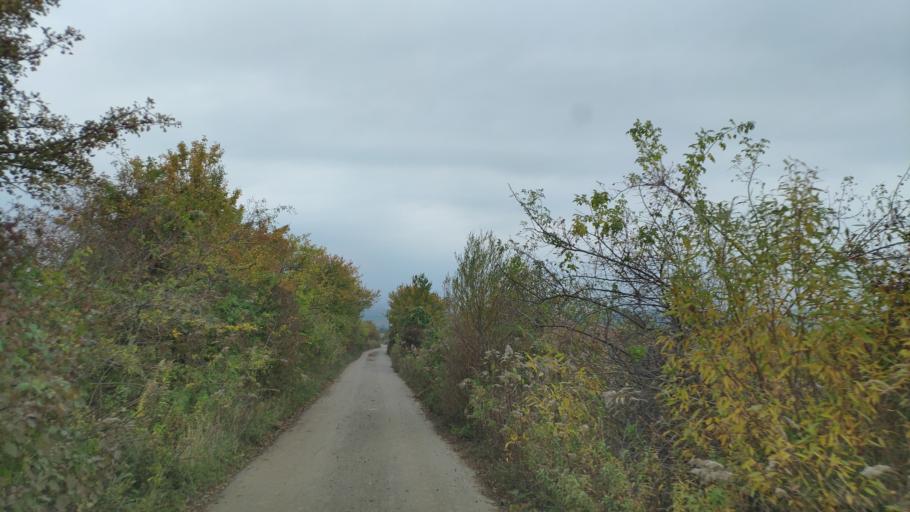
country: SK
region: Kosicky
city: Kosice
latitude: 48.6292
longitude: 21.4047
